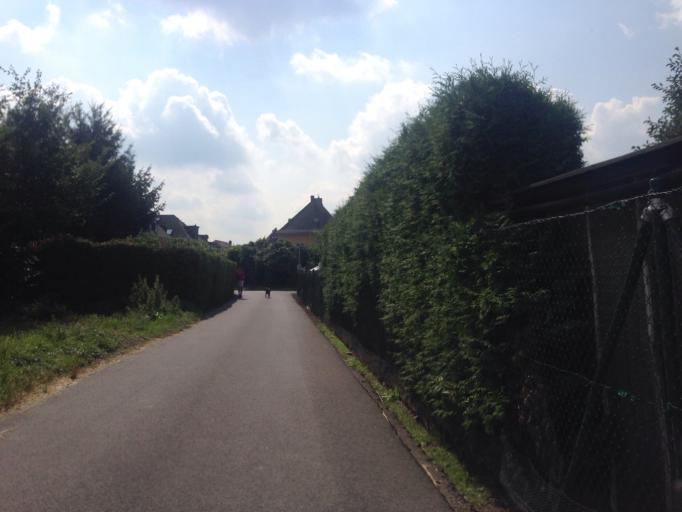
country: DE
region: Hesse
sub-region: Regierungsbezirk Darmstadt
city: Eschborn
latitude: 50.1105
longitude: 8.5815
